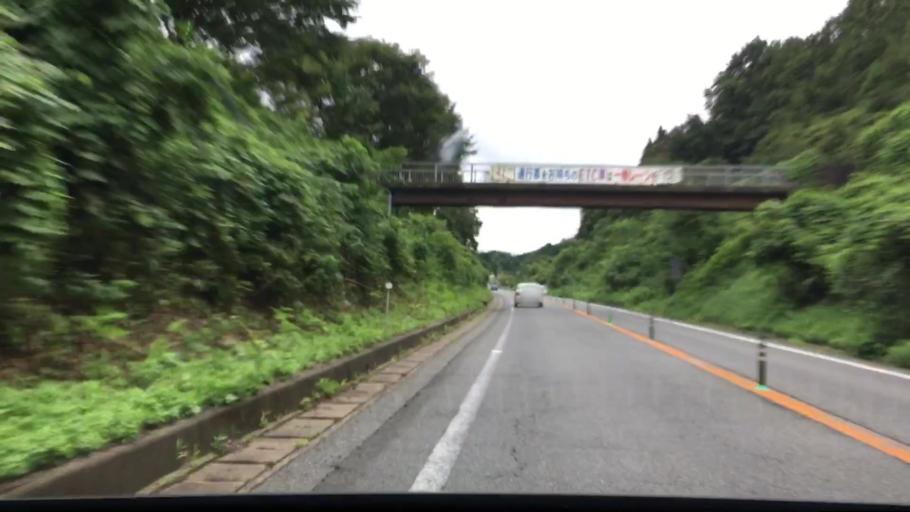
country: JP
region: Hyogo
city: Nishiwaki
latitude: 35.1027
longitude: 134.7776
